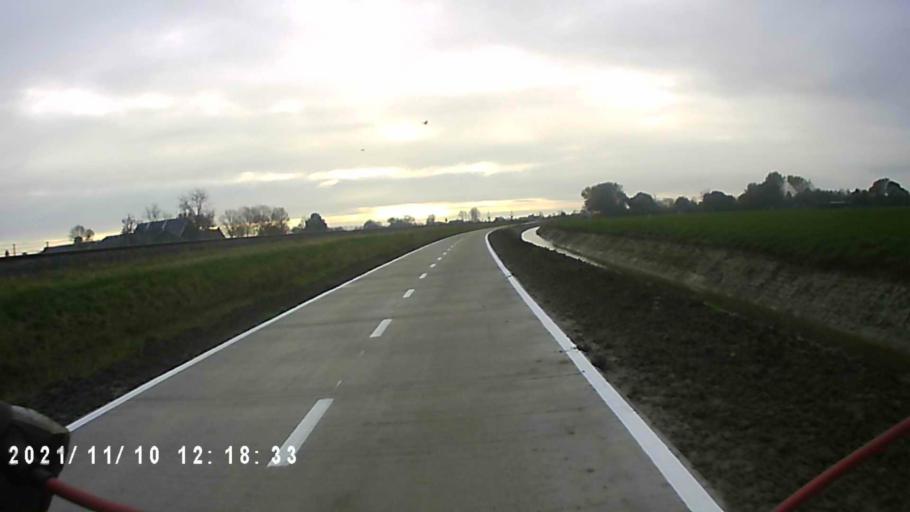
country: NL
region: Groningen
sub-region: Gemeente Winsum
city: Winsum
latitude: 53.2998
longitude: 6.5400
